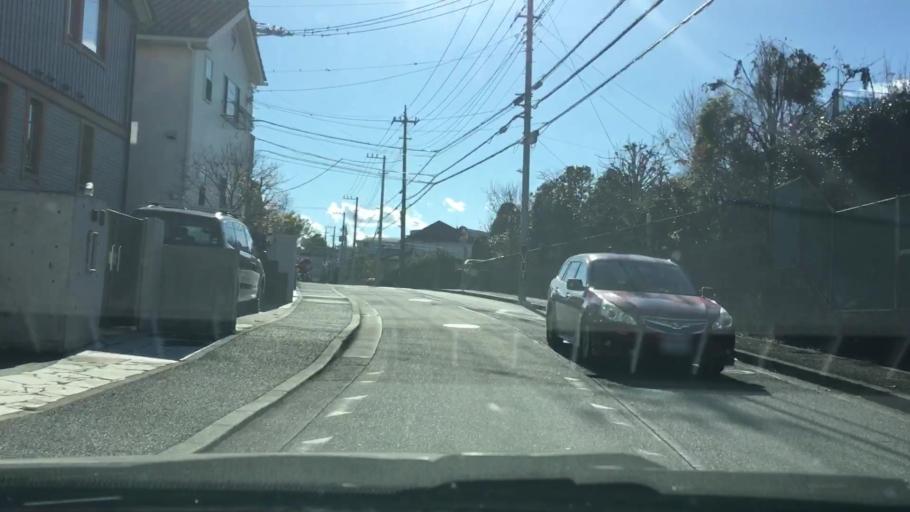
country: JP
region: Tokyo
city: Chofugaoka
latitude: 35.5493
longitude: 139.5662
